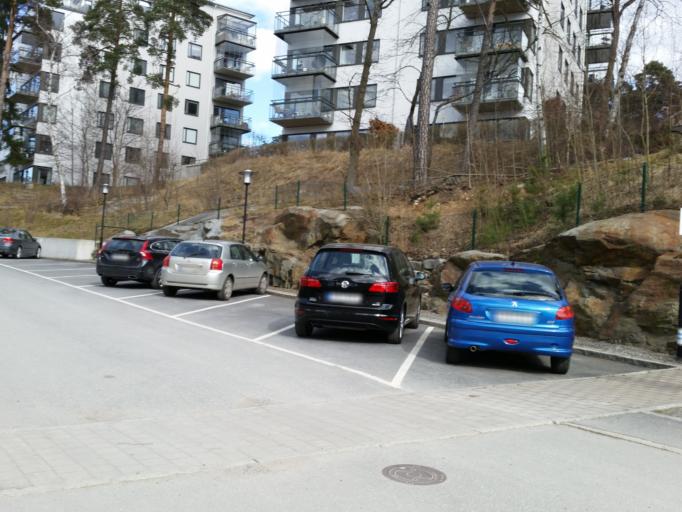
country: SE
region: Stockholm
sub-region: Sundbybergs Kommun
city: Sundbyberg
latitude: 59.3701
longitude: 17.9624
